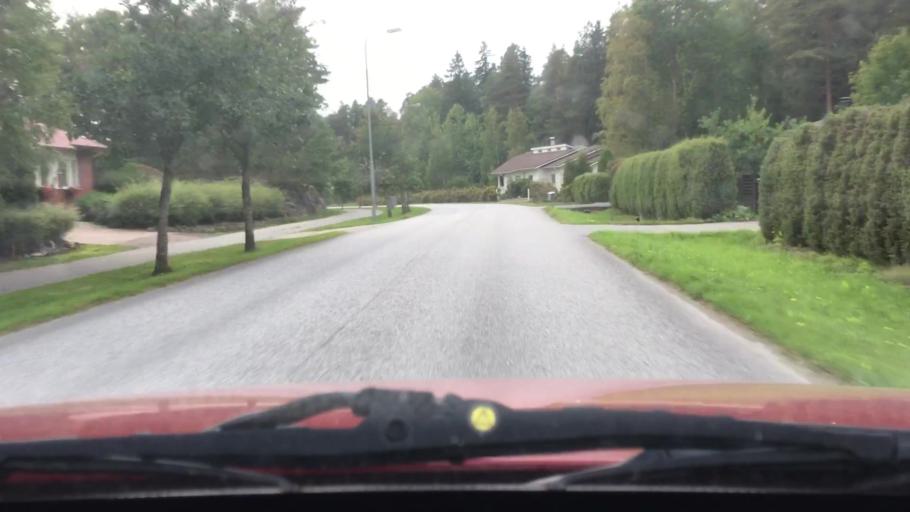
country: FI
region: Varsinais-Suomi
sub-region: Turku
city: Masku
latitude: 60.5582
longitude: 22.1371
